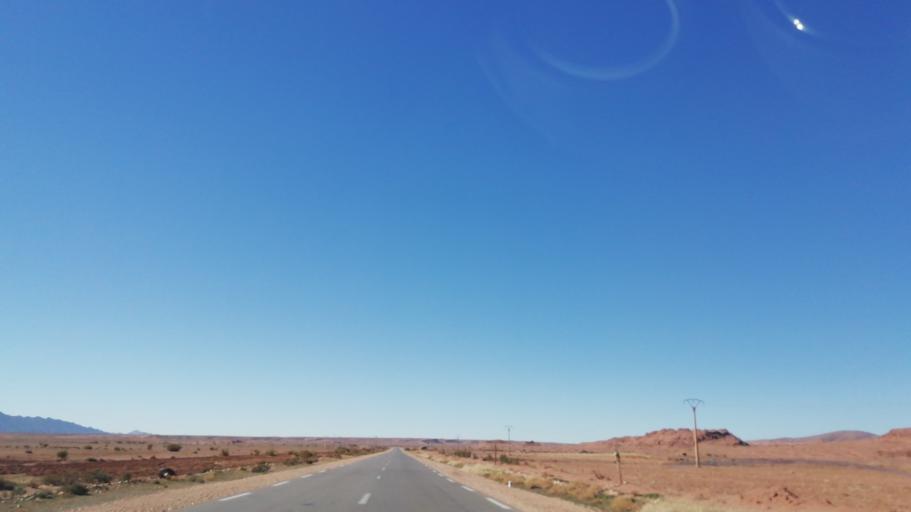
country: DZ
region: El Bayadh
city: El Abiodh Sidi Cheikh
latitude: 33.1769
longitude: 0.5332
